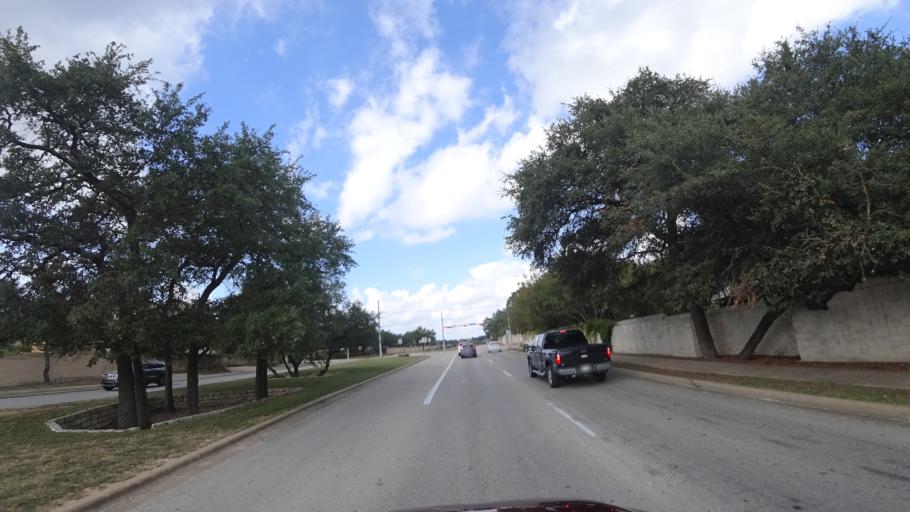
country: US
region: Texas
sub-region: Williamson County
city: Anderson Mill
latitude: 30.4624
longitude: -97.8428
